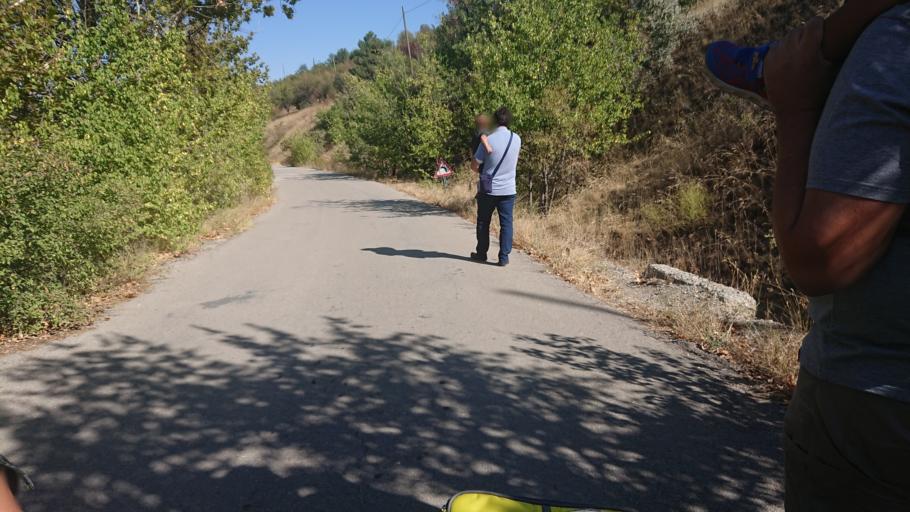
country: TR
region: Ankara
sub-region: Goelbasi
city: Golbasi
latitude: 39.8227
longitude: 32.8234
